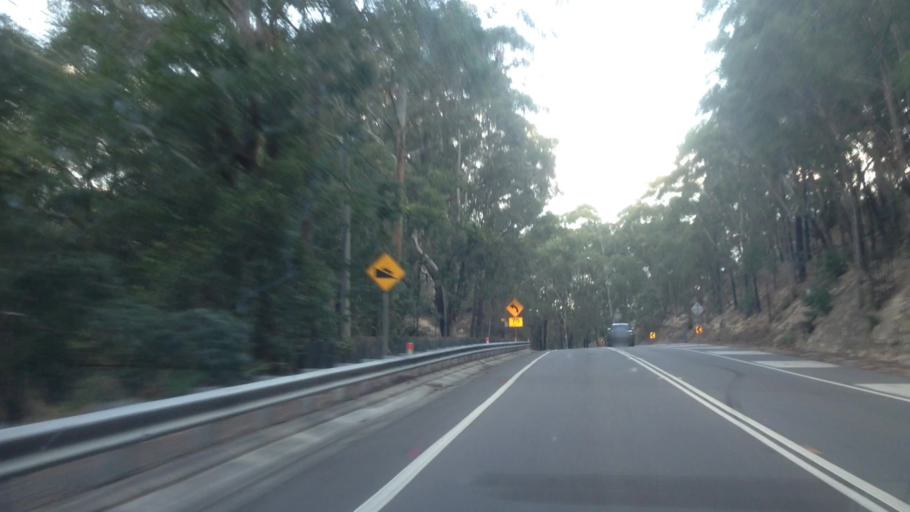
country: AU
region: New South Wales
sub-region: Lake Macquarie Shire
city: Cooranbong
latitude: -32.9672
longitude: 151.4798
